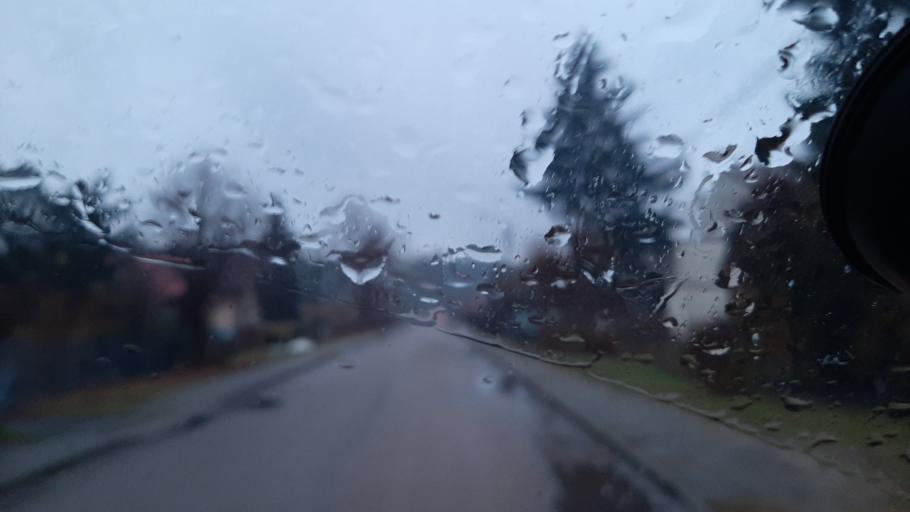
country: PL
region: Lublin Voivodeship
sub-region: Powiat lubartowski
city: Firlej
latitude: 51.5558
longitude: 22.5081
